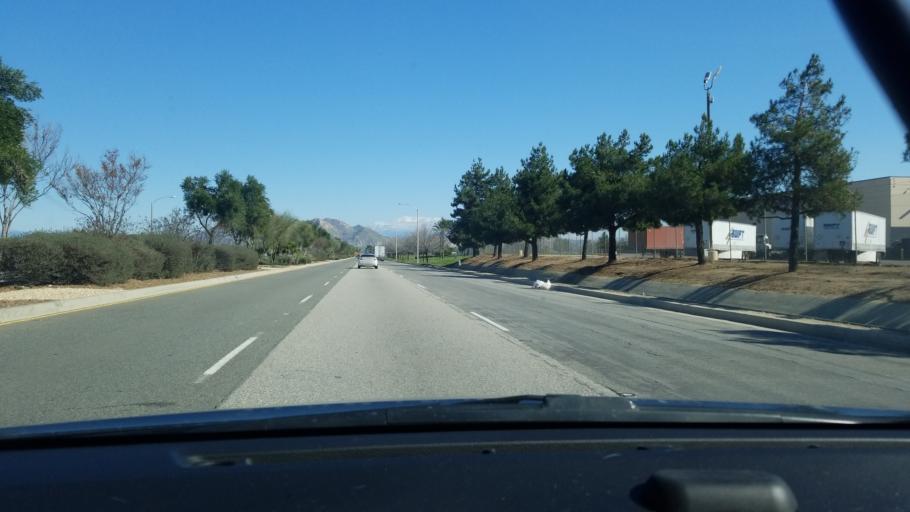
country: US
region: California
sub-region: Riverside County
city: March Air Force Base
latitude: 33.8445
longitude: -117.2375
